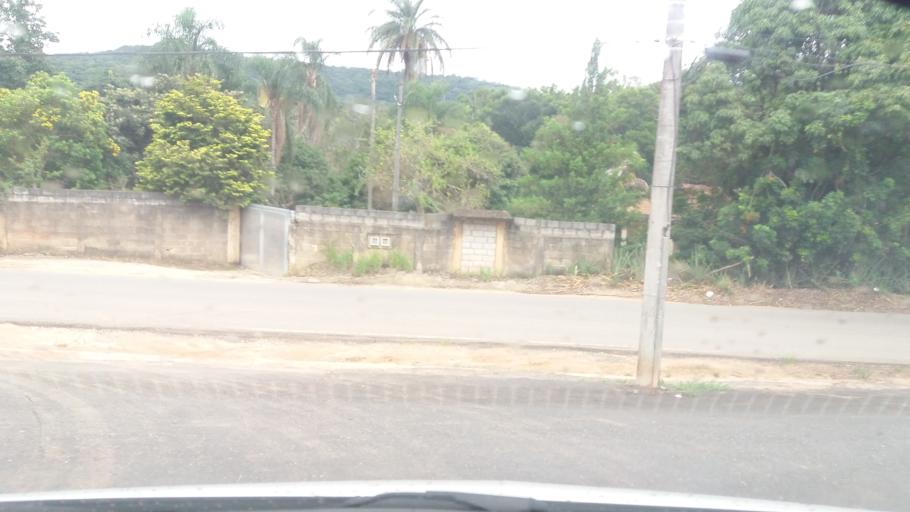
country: BR
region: Sao Paulo
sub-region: Bom Jesus Dos Perdoes
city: Bom Jesus dos Perdoes
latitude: -23.1717
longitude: -46.4384
